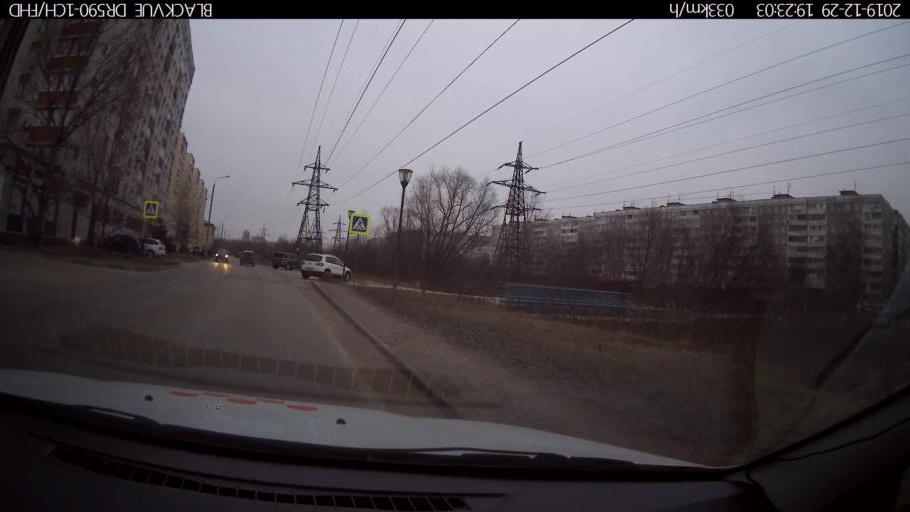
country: RU
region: Nizjnij Novgorod
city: Nizhniy Novgorod
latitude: 56.3312
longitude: 43.8698
